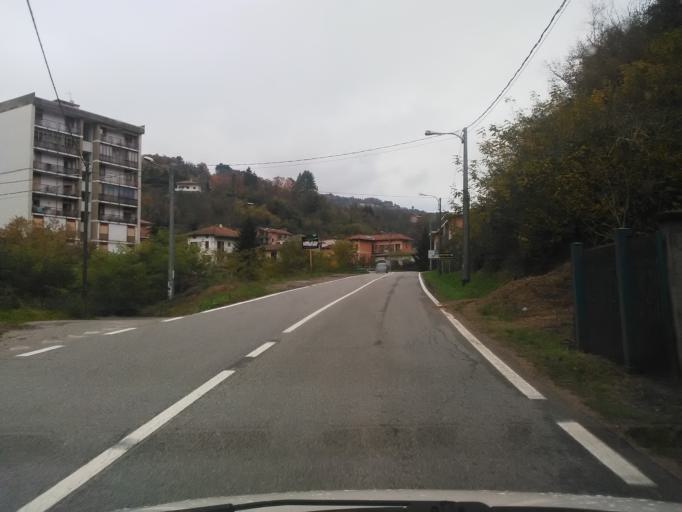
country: IT
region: Piedmont
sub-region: Provincia di Vercelli
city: Valduggia
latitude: 45.7303
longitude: 8.3336
